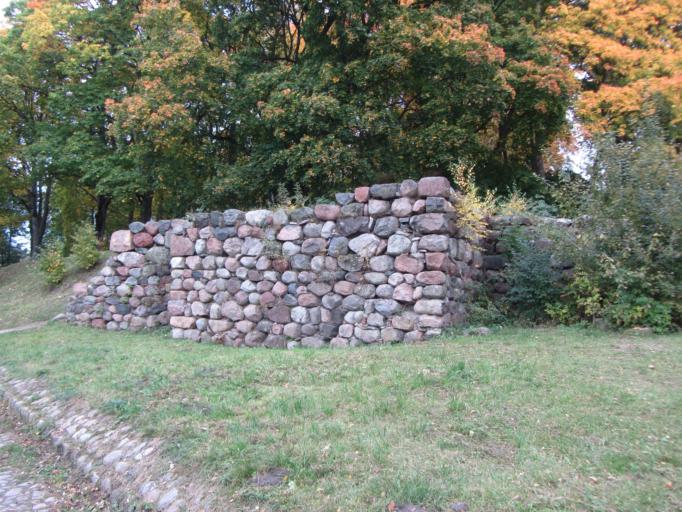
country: LT
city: Trakai
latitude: 54.6469
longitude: 24.9368
